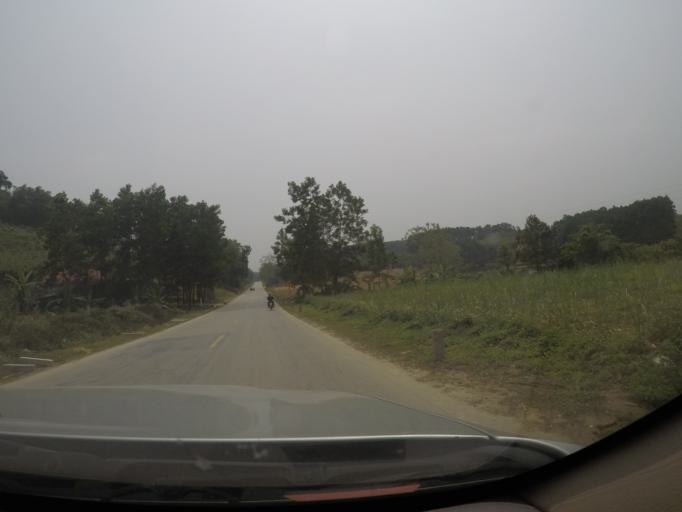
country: VN
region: Thanh Hoa
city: Thi Tran Thuong Xuan
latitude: 19.8237
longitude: 105.3904
